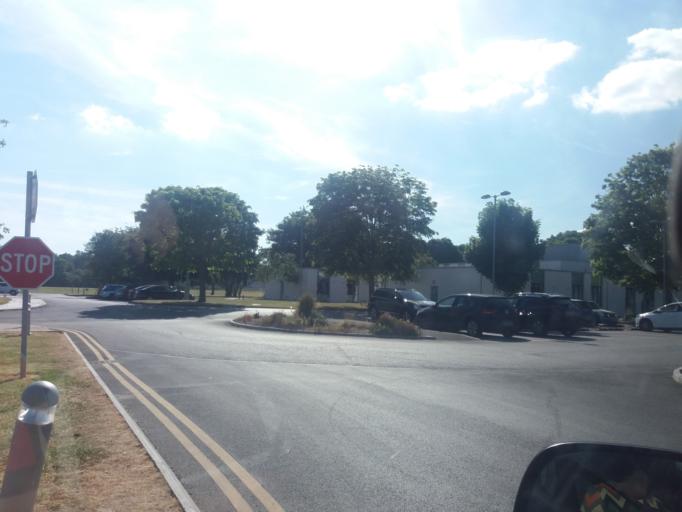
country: IE
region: Leinster
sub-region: Fingal County
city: Blanchardstown
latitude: 53.3961
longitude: -6.3556
